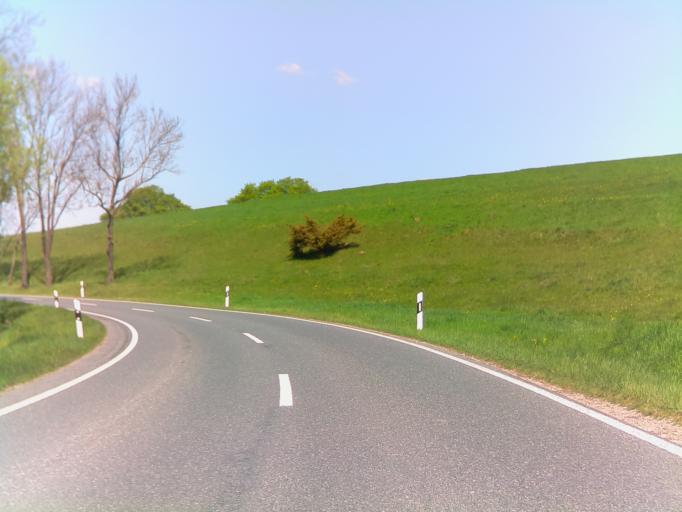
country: DE
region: Thuringia
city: Stadtilm
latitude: 50.7408
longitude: 11.0671
